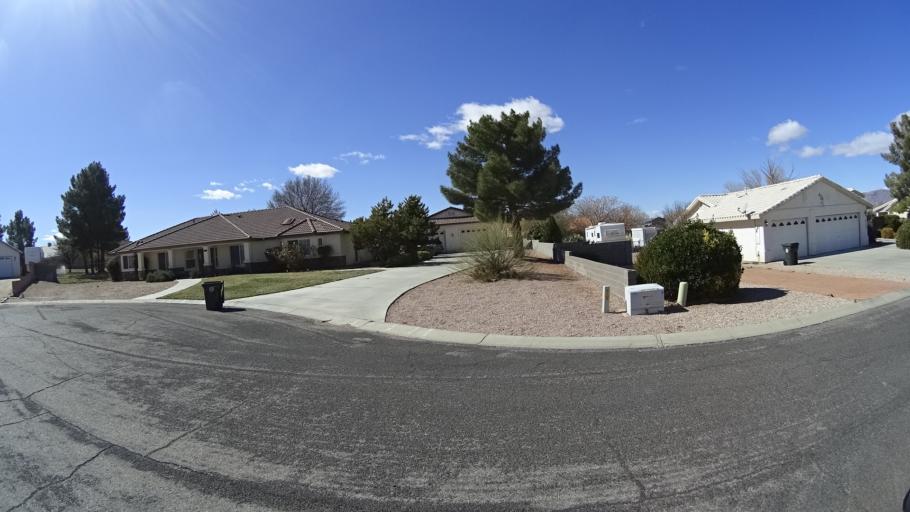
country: US
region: Arizona
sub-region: Mohave County
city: Kingman
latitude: 35.2023
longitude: -113.9634
